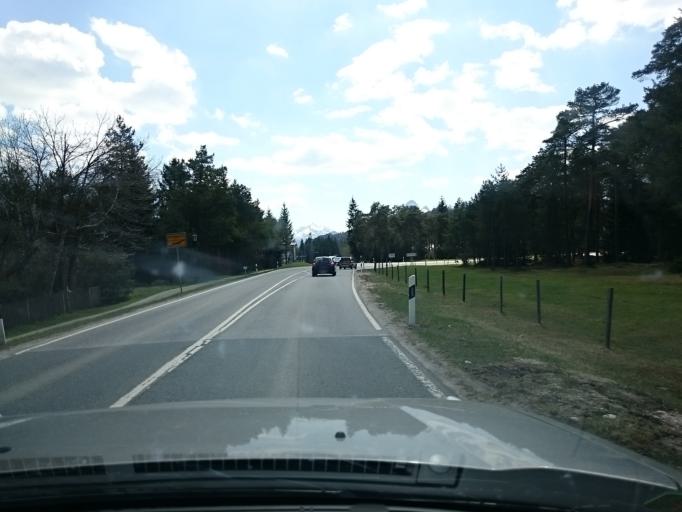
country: DE
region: Bavaria
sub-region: Upper Bavaria
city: Krun
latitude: 47.4985
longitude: 11.2778
